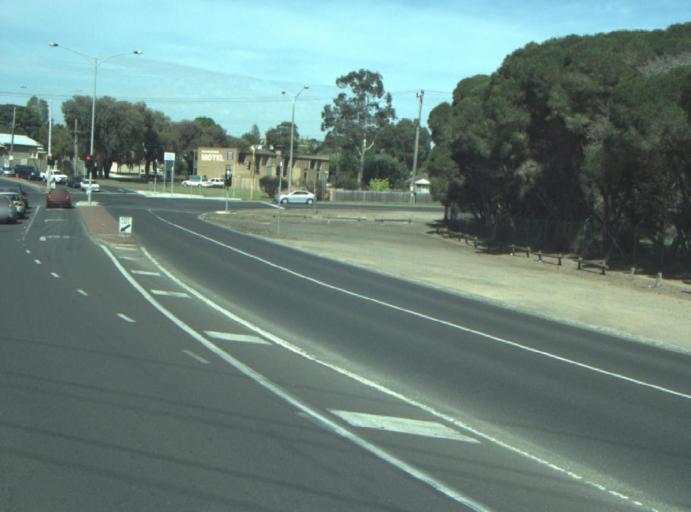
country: AU
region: Victoria
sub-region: Greater Geelong
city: Hamlyn Heights
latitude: -38.1263
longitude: 144.3403
